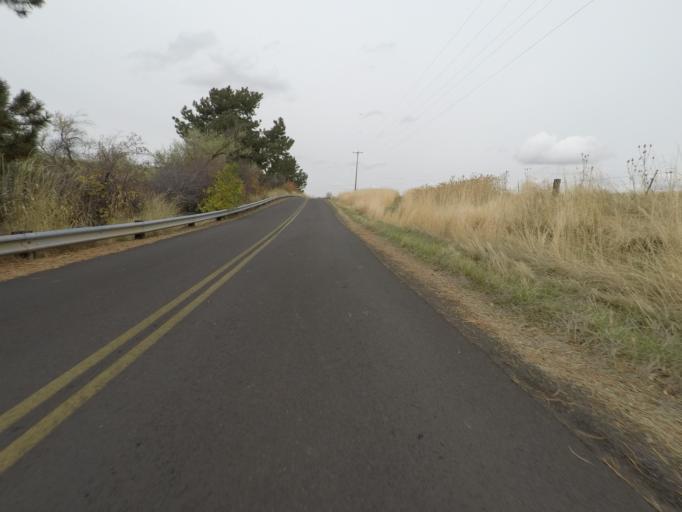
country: US
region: Washington
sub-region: Walla Walla County
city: Walla Walla East
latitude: 46.0705
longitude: -118.2696
